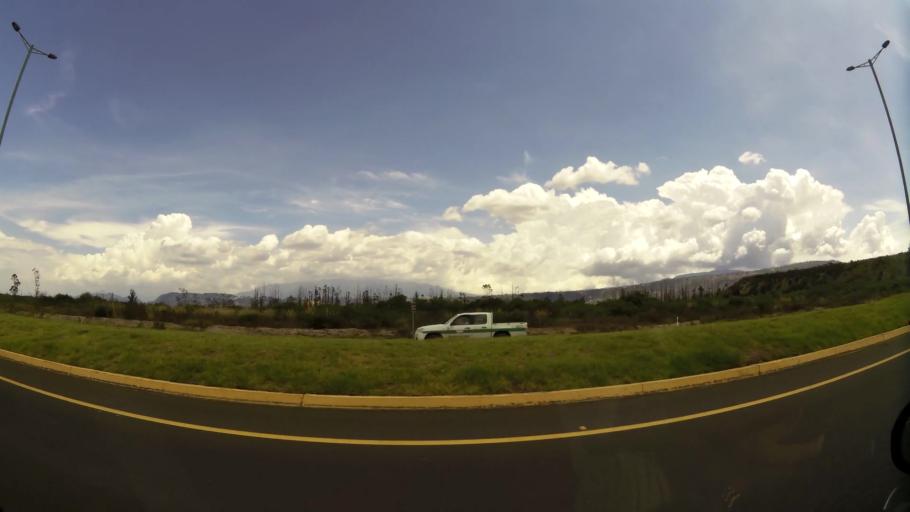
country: EC
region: Pichincha
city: Quito
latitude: -0.1140
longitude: -78.3655
